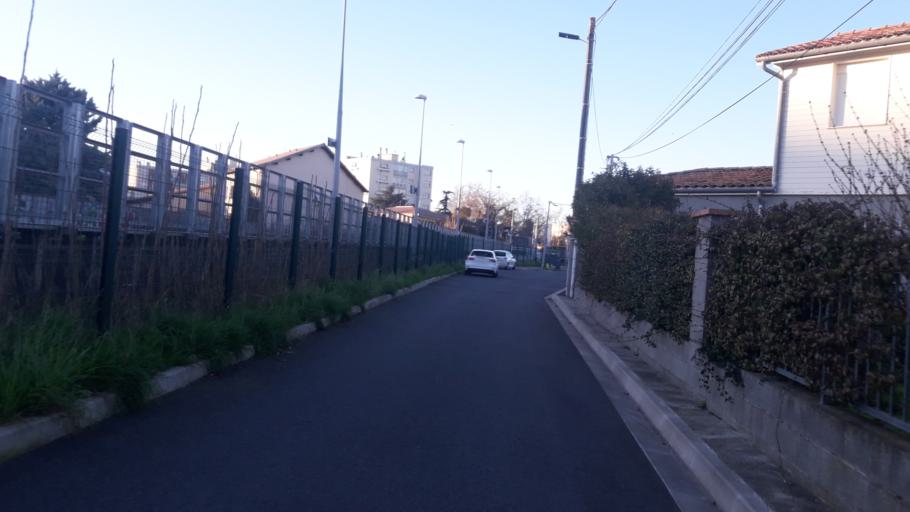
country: FR
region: Midi-Pyrenees
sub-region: Departement de la Haute-Garonne
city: Toulouse
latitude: 43.5721
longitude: 1.4203
